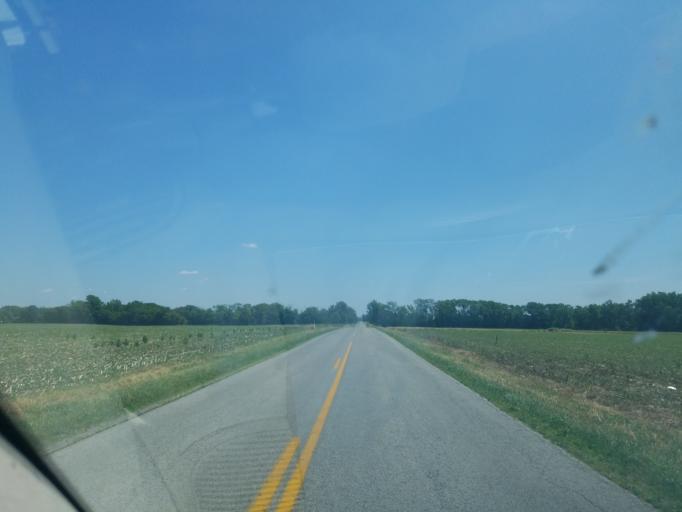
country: US
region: Ohio
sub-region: Allen County
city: Delphos
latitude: 40.7867
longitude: -84.2981
